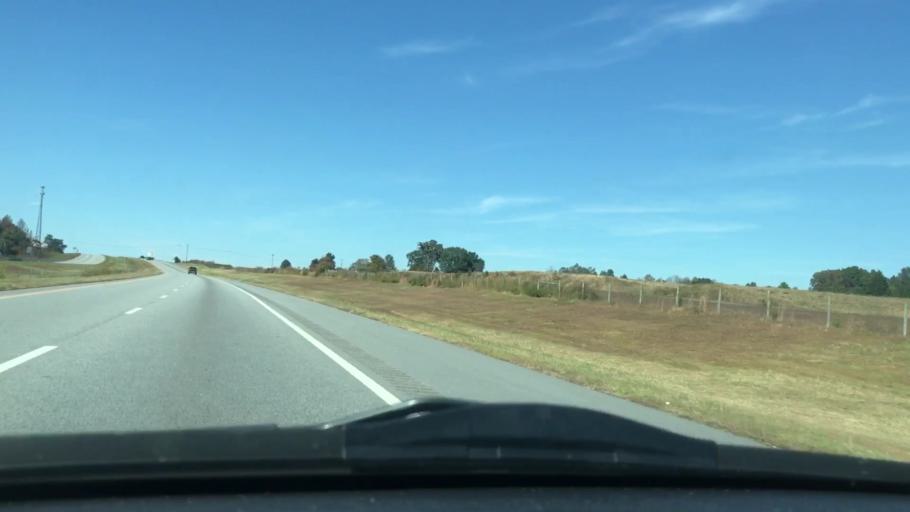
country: US
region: North Carolina
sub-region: Randolph County
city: Archdale
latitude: 35.8652
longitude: -79.8912
